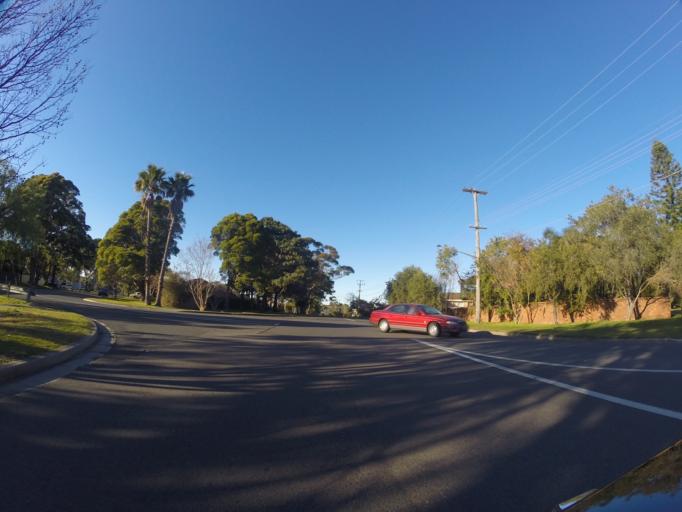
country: AU
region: New South Wales
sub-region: Sutherland Shire
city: Miranda
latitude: -34.0442
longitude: 151.1004
